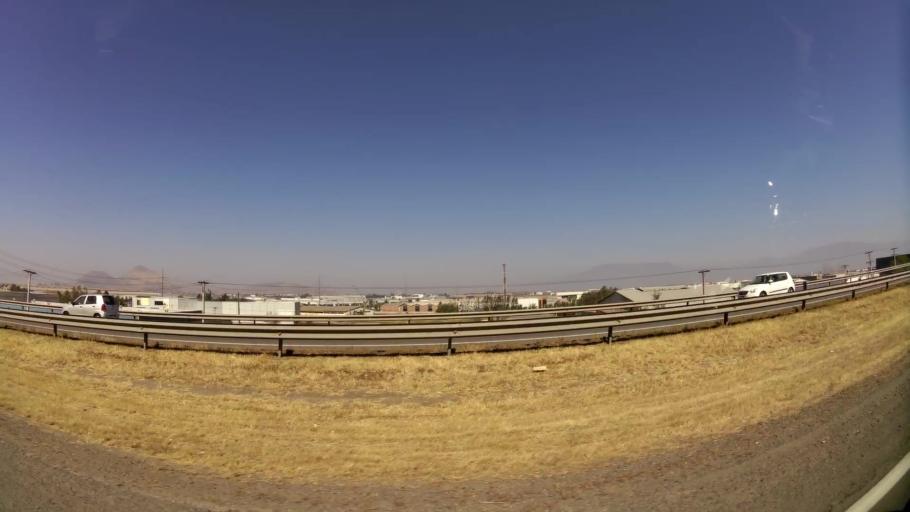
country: CL
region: Santiago Metropolitan
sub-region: Provincia de Chacabuco
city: Chicureo Abajo
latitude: -33.3273
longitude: -70.7016
